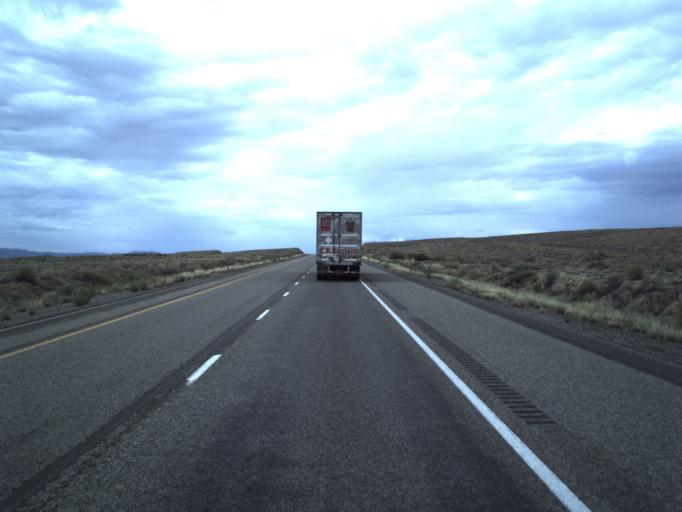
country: US
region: Colorado
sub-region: Mesa County
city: Loma
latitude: 39.1381
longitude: -109.1562
